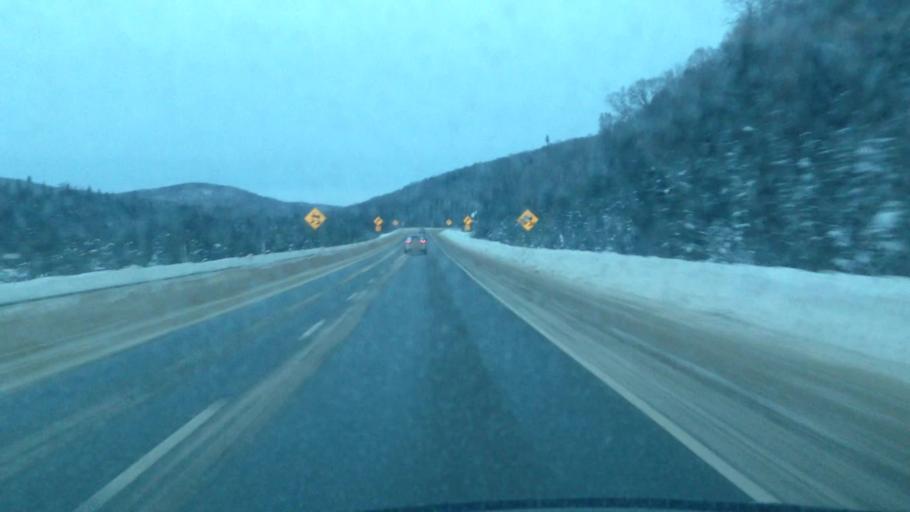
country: CA
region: Quebec
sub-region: Laurentides
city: Mont-Tremblant
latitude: 46.1244
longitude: -74.4394
